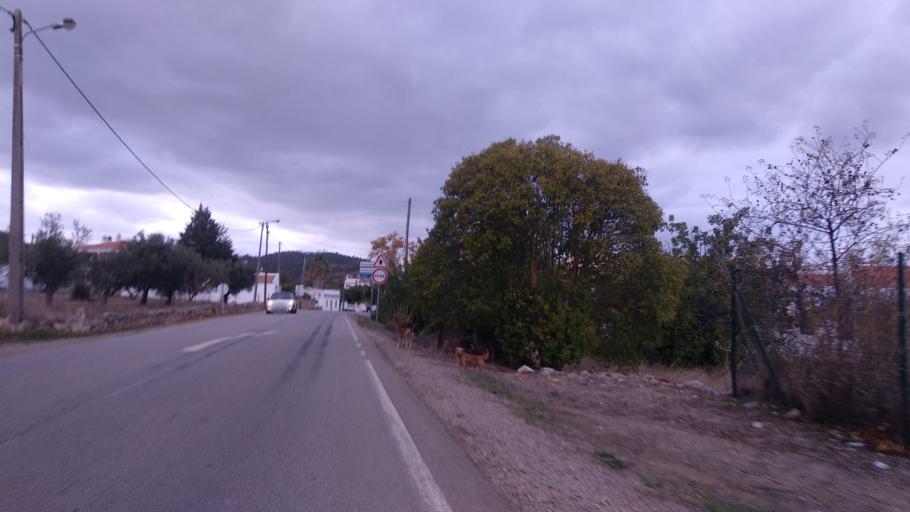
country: PT
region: Faro
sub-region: Sao Bras de Alportel
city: Sao Bras de Alportel
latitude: 37.1674
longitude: -7.9059
